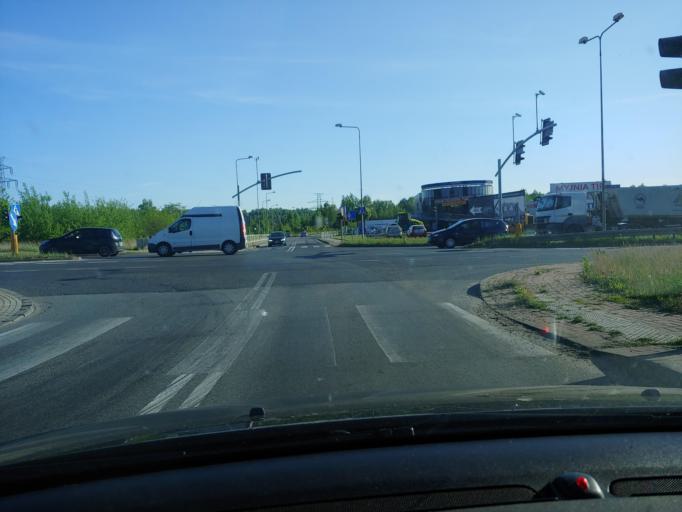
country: PL
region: Silesian Voivodeship
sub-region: Jaworzno
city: Jaworzno
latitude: 50.1856
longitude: 19.2870
